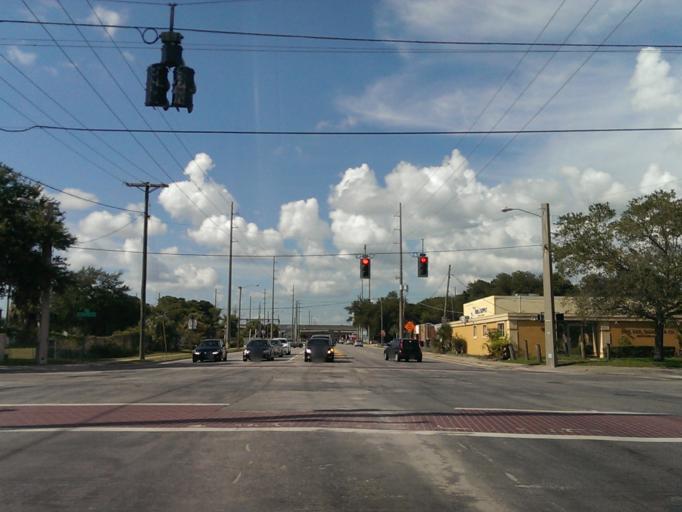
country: US
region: Florida
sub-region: Hillsborough County
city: Tampa
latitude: 27.9519
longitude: -82.5015
